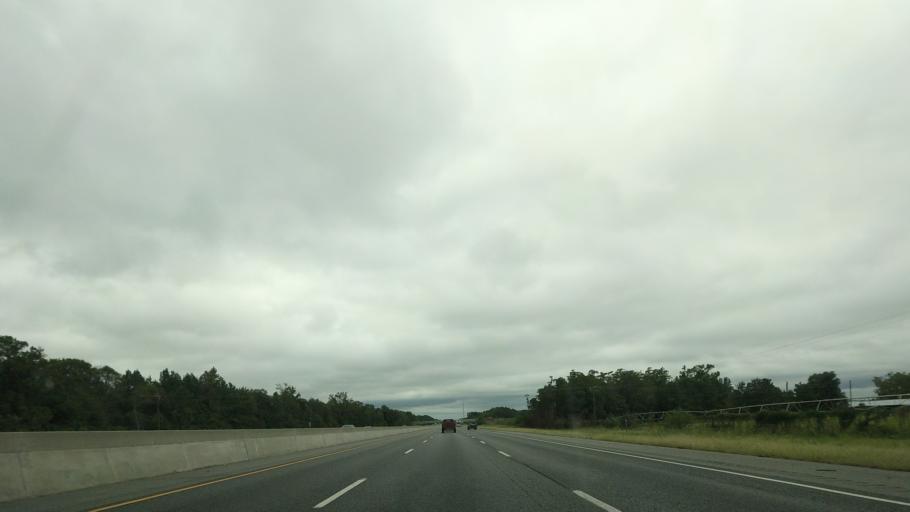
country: US
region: Georgia
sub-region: Lowndes County
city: Hahira
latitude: 30.9553
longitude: -83.3769
